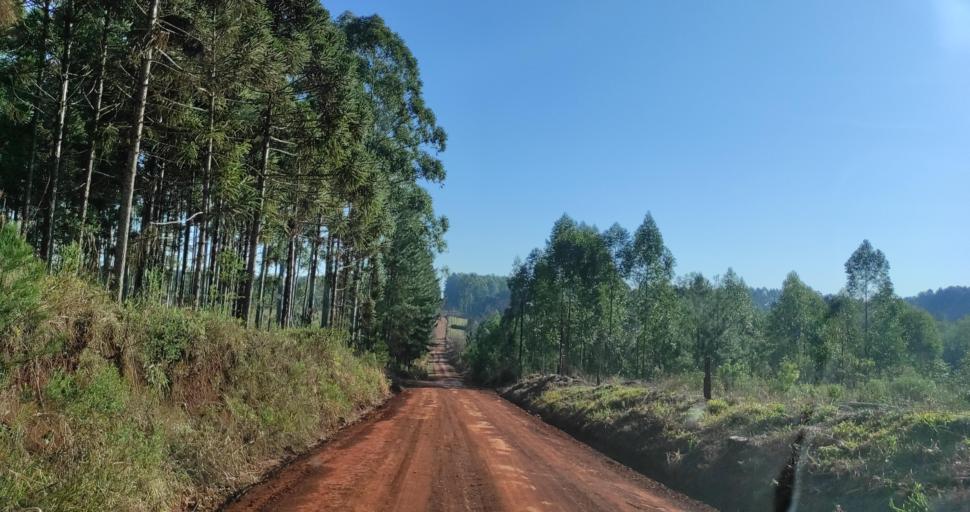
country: AR
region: Misiones
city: Capiovi
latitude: -26.8715
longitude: -55.0158
